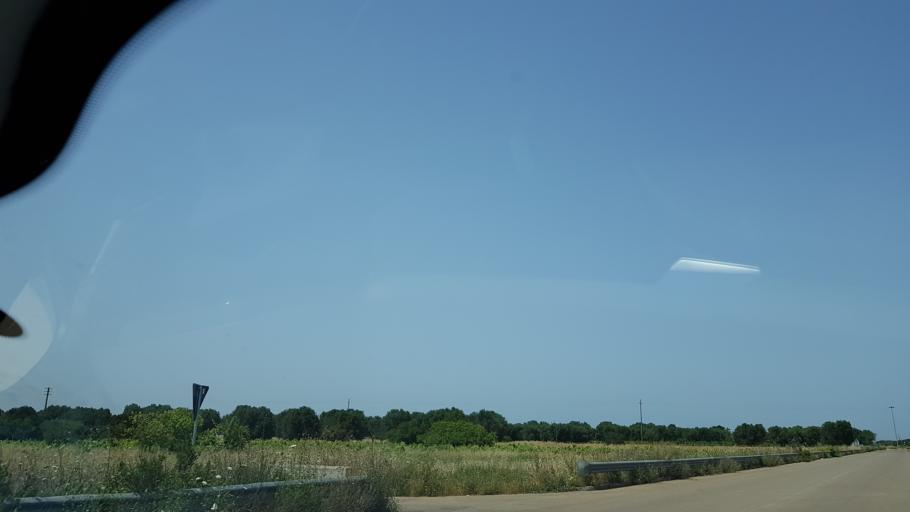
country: IT
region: Apulia
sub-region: Provincia di Brindisi
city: Mesagne
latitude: 40.5542
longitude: 17.8346
